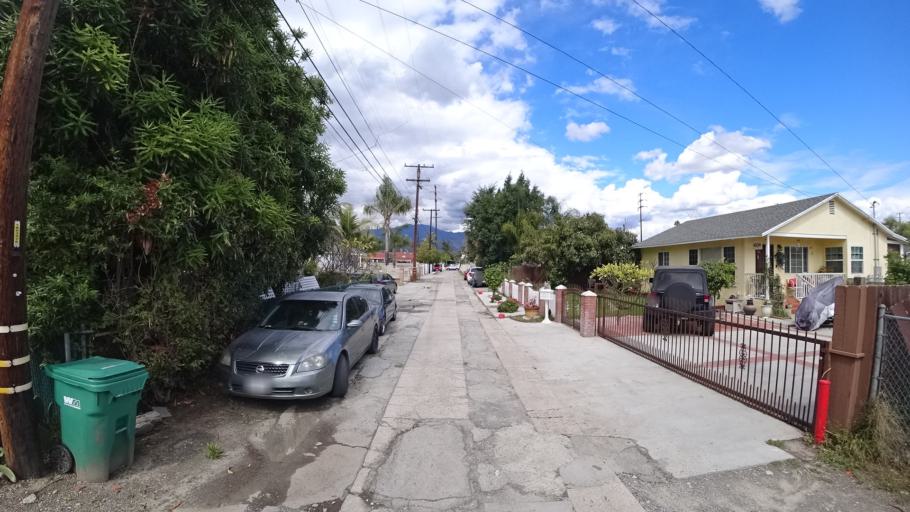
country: US
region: California
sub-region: Los Angeles County
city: Baldwin Park
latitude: 34.0914
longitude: -117.9565
